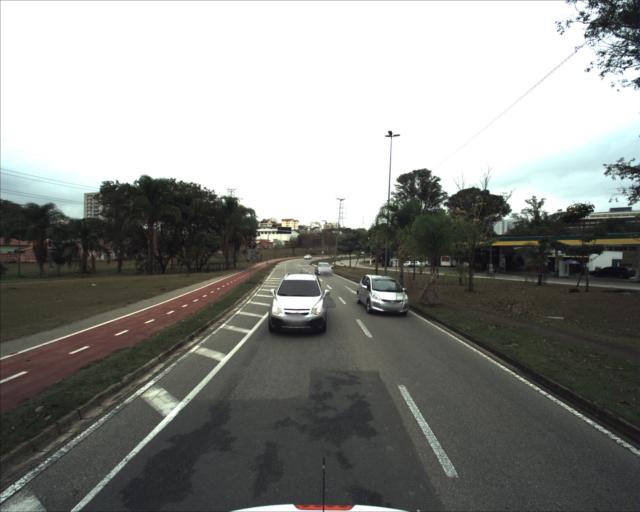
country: BR
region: Sao Paulo
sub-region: Sorocaba
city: Sorocaba
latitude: -23.5113
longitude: -47.4539
